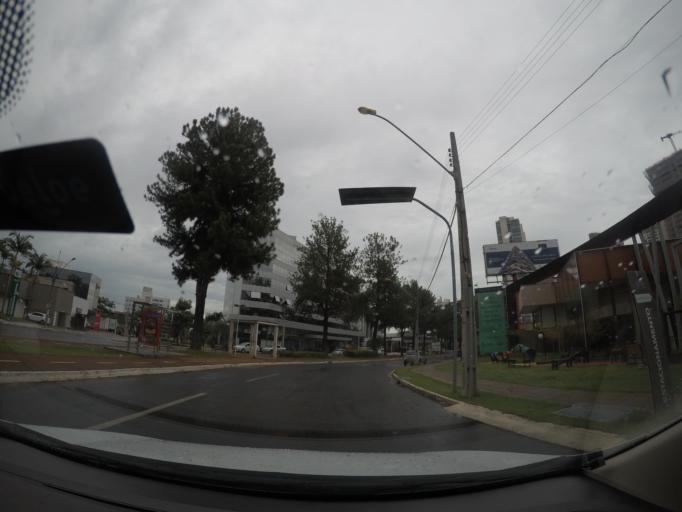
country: BR
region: Goias
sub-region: Goiania
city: Goiania
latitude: -16.7014
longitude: -49.2570
